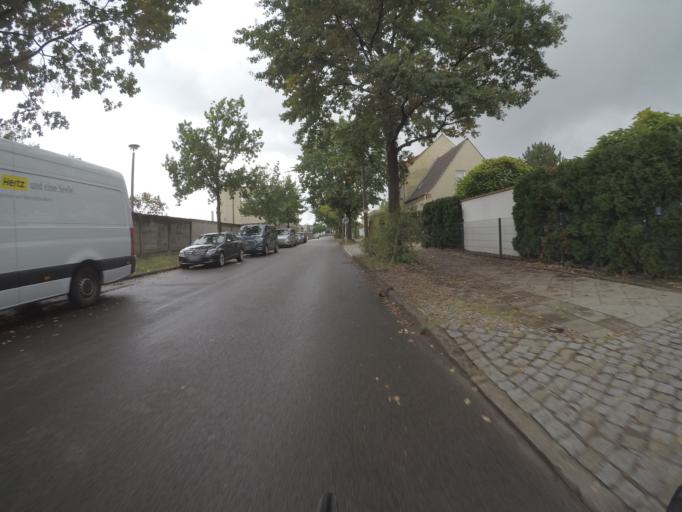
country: DE
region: Berlin
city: Buchholz
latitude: 52.5896
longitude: 13.4208
